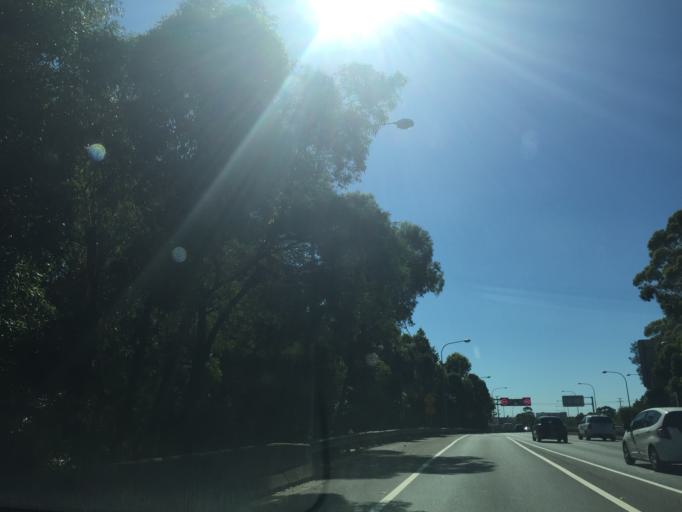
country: AU
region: New South Wales
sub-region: Strathfield
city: Homebush
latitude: -33.8655
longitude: 151.0925
